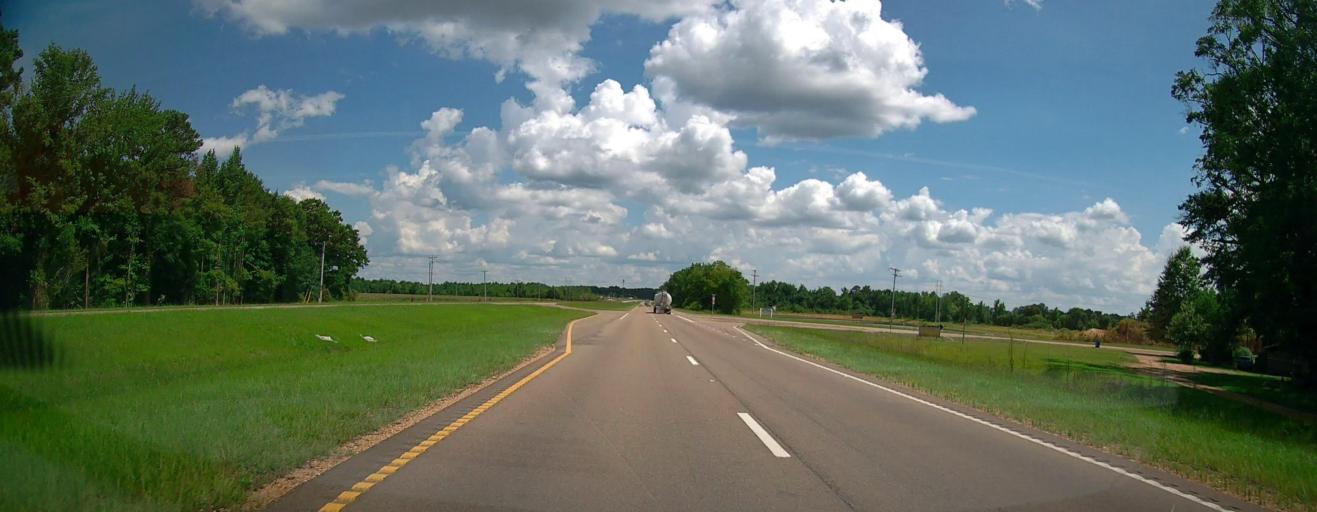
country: US
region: Mississippi
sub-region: Lowndes County
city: Columbus Air Force Base
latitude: 33.6664
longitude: -88.4251
